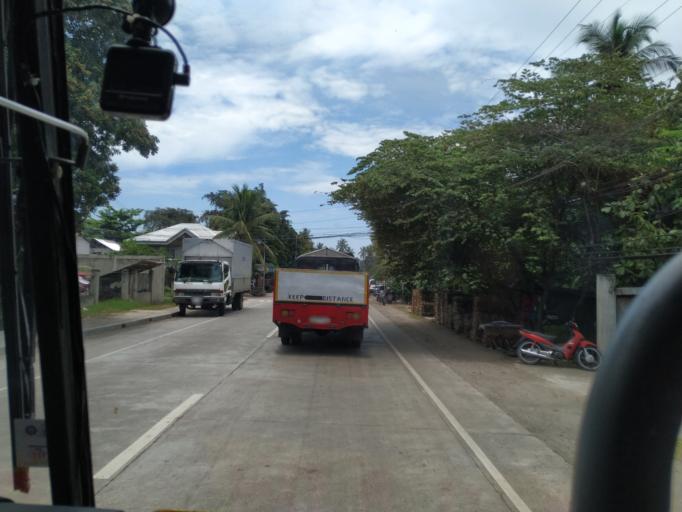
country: PH
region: Central Visayas
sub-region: Province of Negros Oriental
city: Sibulan
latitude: 9.3508
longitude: 123.2853
